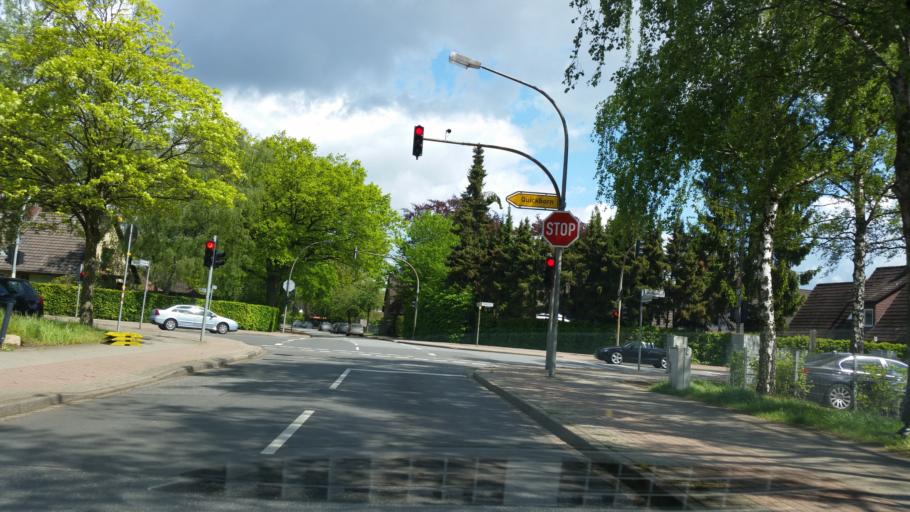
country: DE
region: Schleswig-Holstein
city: Norderstedt
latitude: 53.7141
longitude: 9.9874
